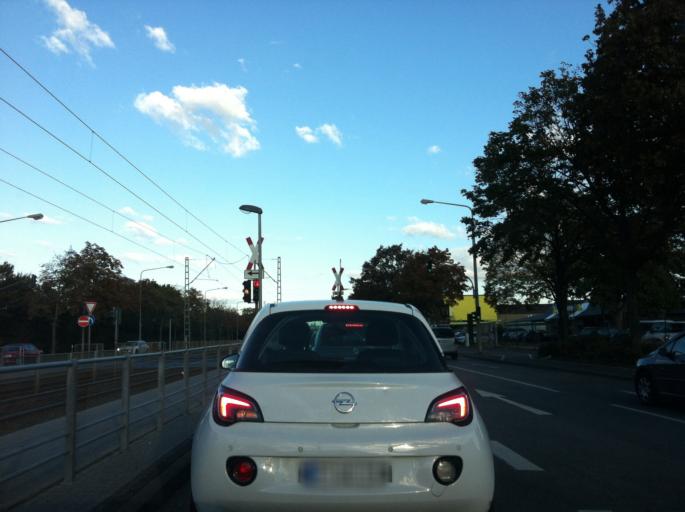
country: DE
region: Hesse
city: Niederrad
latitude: 50.1002
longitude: 8.6049
